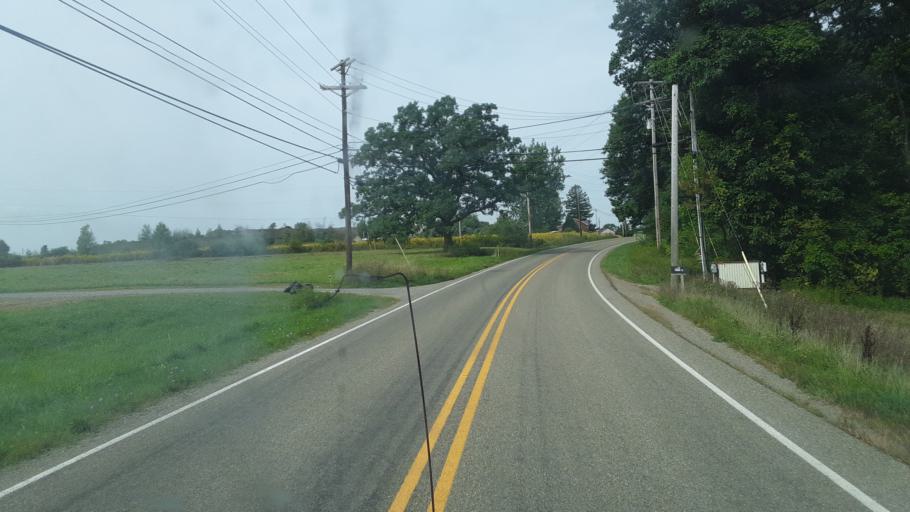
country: US
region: Pennsylvania
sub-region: Jefferson County
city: Punxsutawney
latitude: 40.9643
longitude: -79.0956
